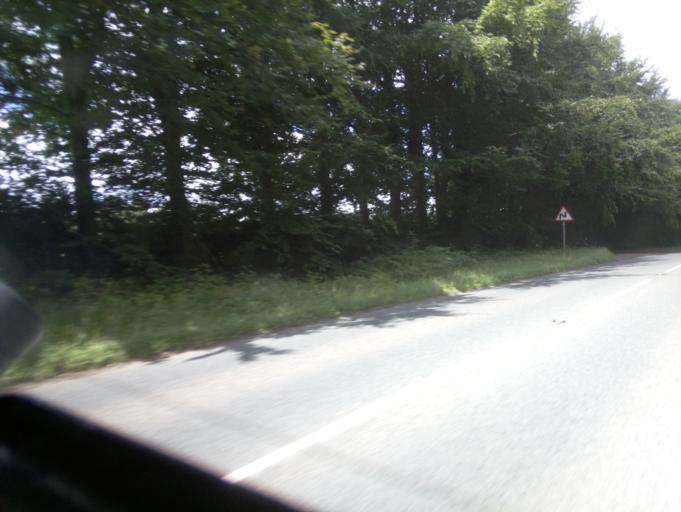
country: GB
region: England
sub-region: Gloucestershire
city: Lydney
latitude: 51.7336
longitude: -2.5470
